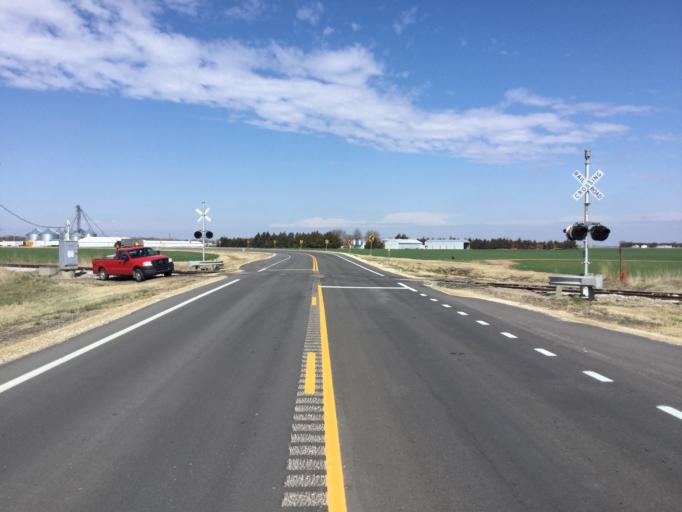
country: US
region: Kansas
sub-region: Barton County
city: Ellinwood
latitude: 38.3519
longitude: -98.5592
